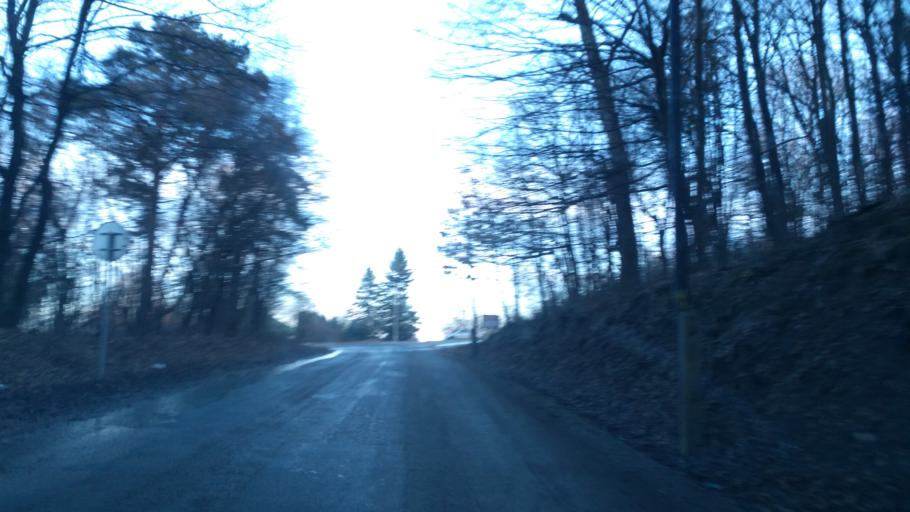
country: SK
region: Kosicky
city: Kosice
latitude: 48.7450
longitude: 21.2085
